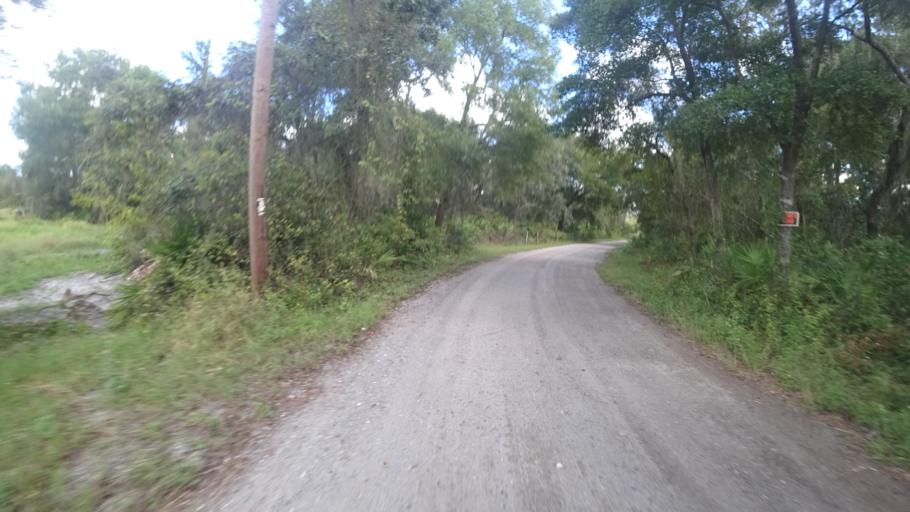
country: US
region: Florida
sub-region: Sarasota County
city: Lake Sarasota
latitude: 27.3283
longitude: -82.2652
